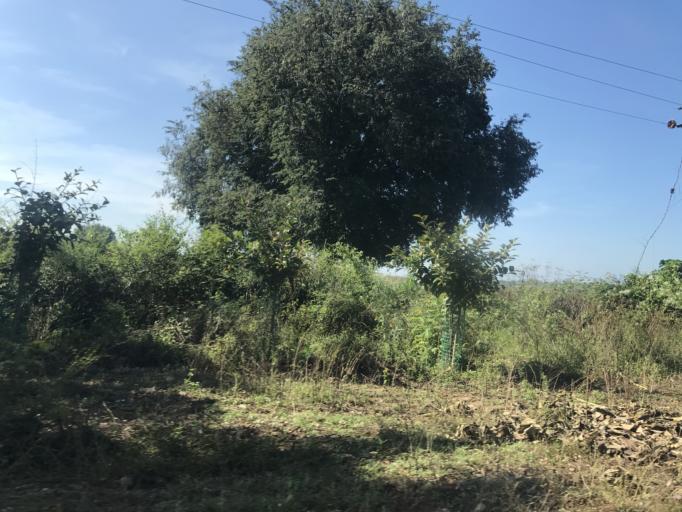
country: IN
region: Karnataka
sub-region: Mysore
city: Heggadadevankote
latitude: 12.0155
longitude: 76.2676
